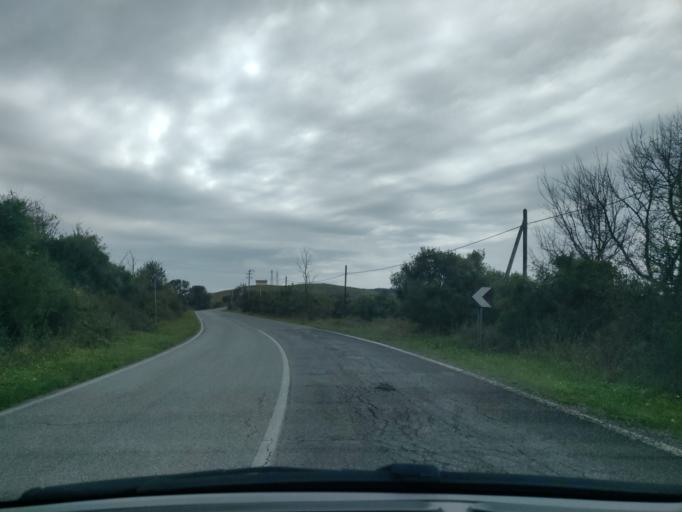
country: IT
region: Latium
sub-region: Citta metropolitana di Roma Capitale
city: Allumiere
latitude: 42.1193
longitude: 11.8615
